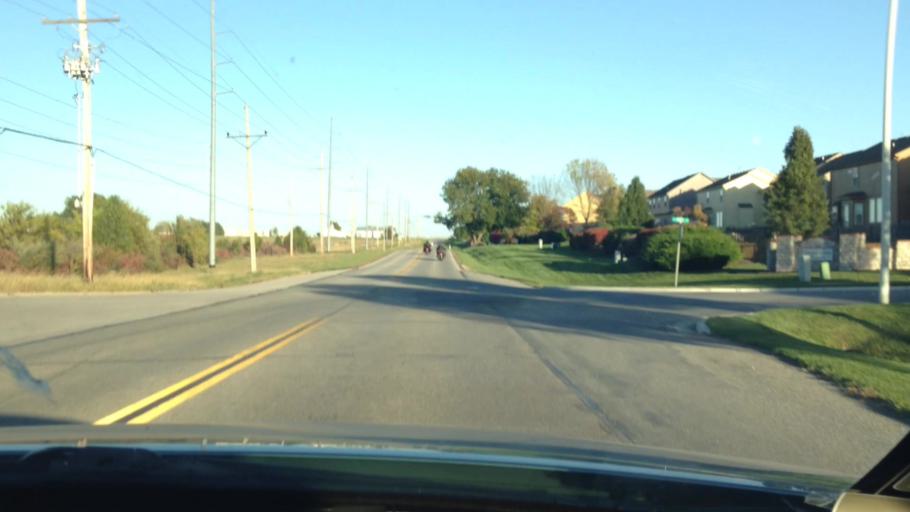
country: US
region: Kansas
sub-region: Johnson County
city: Gardner
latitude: 38.8255
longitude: -94.9173
